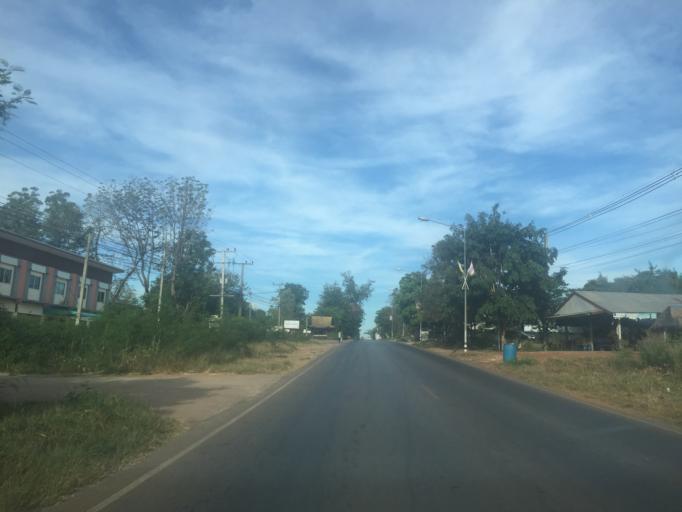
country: TH
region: Changwat Udon Thani
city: Si That
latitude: 16.9805
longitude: 103.1869
